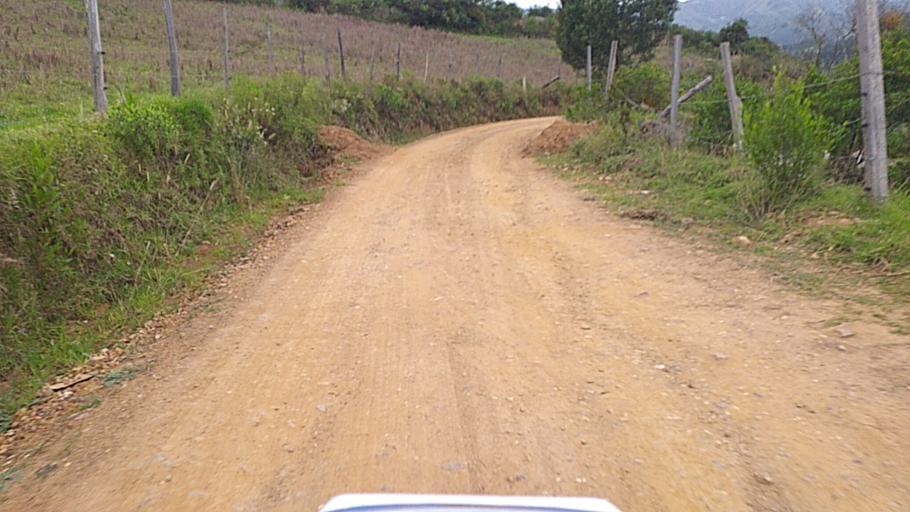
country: CO
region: Boyaca
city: Floresta
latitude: 5.8778
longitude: -72.9135
